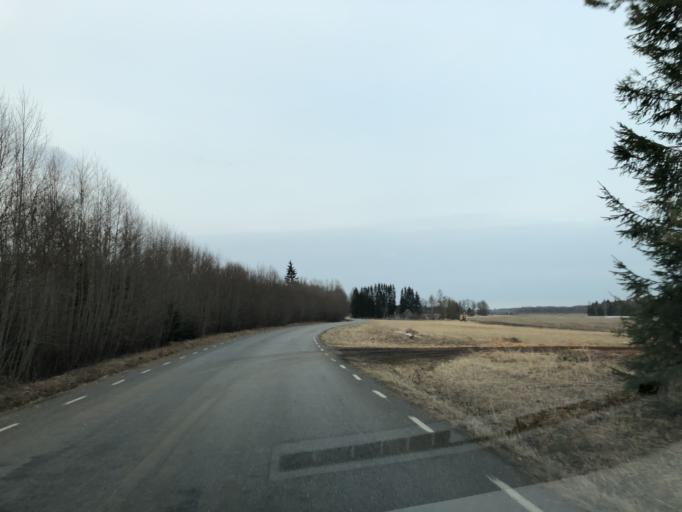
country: EE
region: Paernumaa
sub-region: Vaendra vald (alev)
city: Vandra
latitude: 58.6977
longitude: 24.9344
